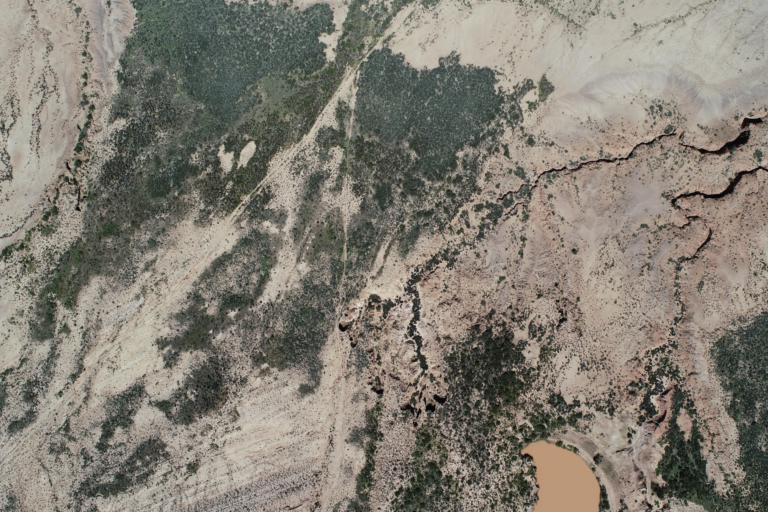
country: BO
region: La Paz
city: Patacamaya
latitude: -17.2952
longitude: -68.4920
